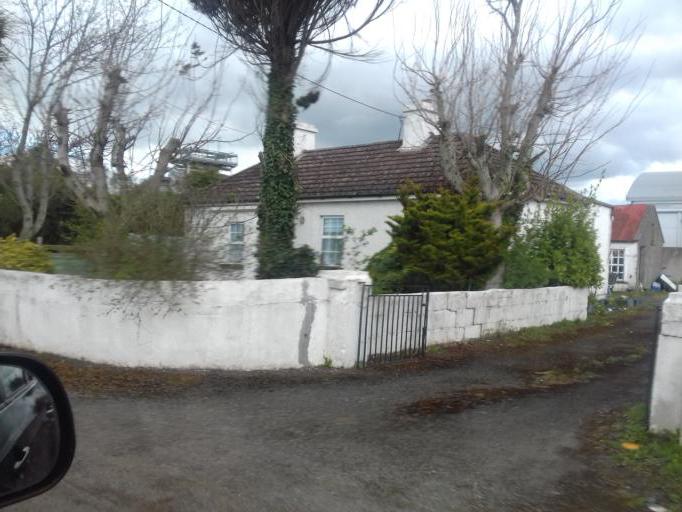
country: IE
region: Leinster
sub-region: Fingal County
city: Swords
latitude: 53.4438
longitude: -6.2208
